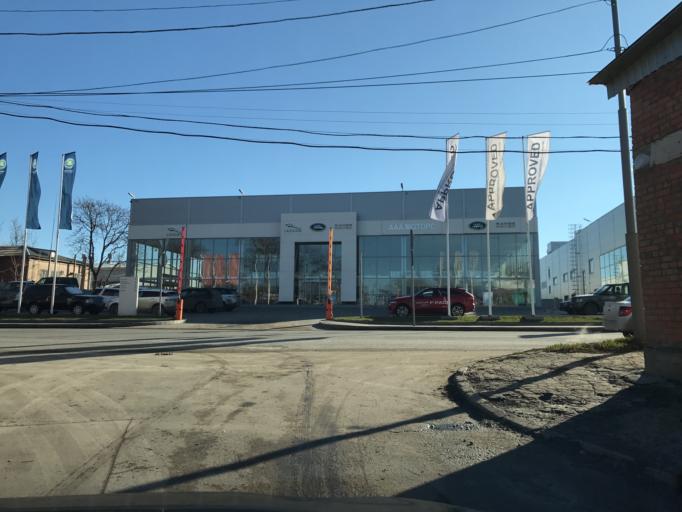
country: RU
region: Rostov
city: Rostov-na-Donu
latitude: 47.2419
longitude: 39.7396
